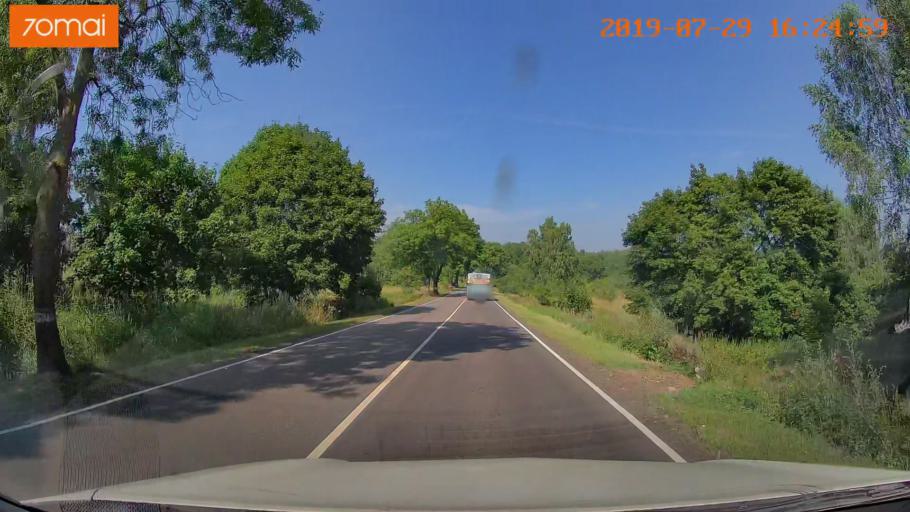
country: RU
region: Kaliningrad
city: Primorsk
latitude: 54.7192
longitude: 19.9619
